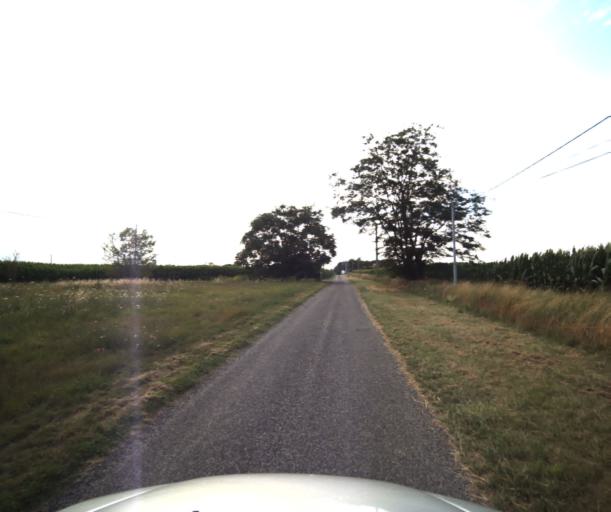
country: FR
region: Midi-Pyrenees
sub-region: Departement de la Haute-Garonne
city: Le Fauga
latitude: 43.4250
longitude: 1.3131
